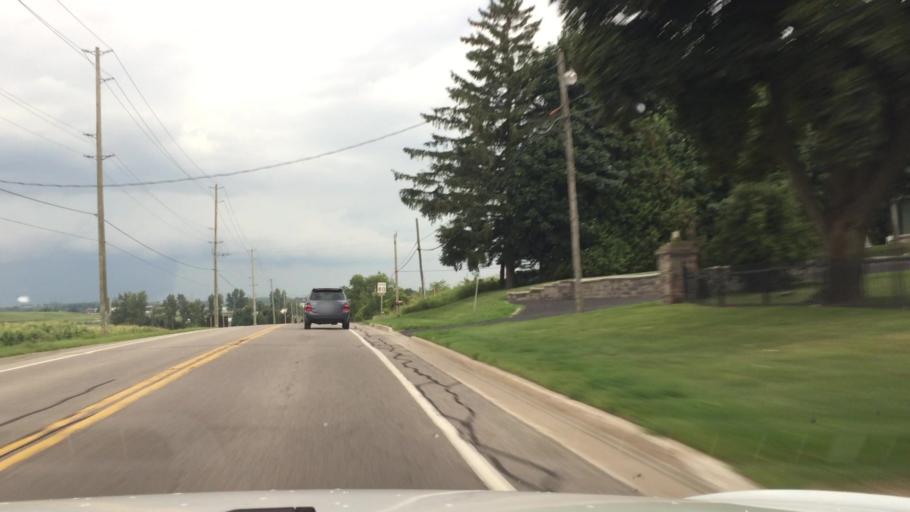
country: CA
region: Ontario
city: Oshawa
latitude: 43.9533
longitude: -78.8070
